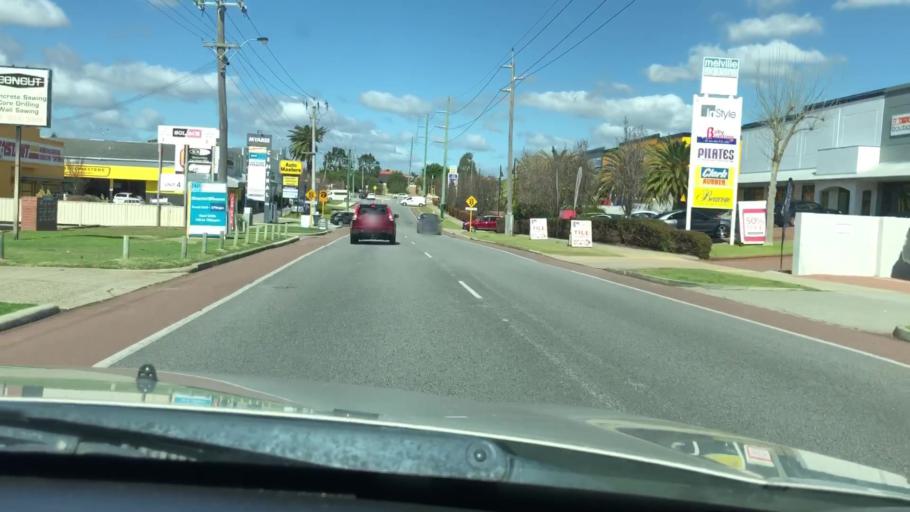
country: AU
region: Western Australia
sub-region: Melville
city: Myaree
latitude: -32.0441
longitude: 115.8223
